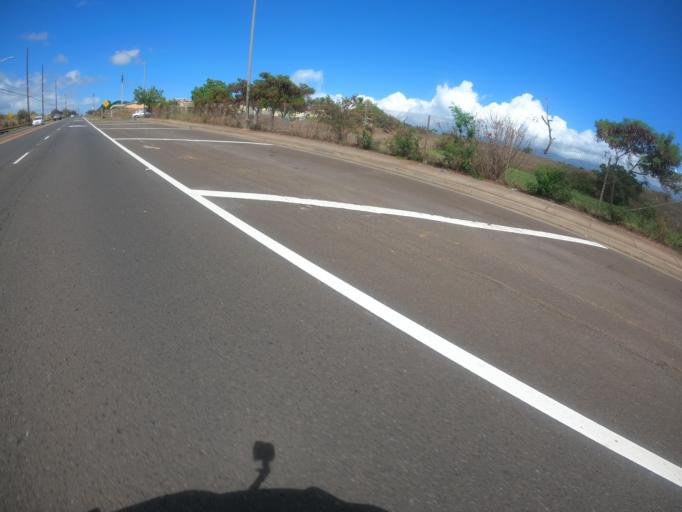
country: US
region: Hawaii
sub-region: Honolulu County
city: Village Park
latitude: 21.3977
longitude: -158.0385
